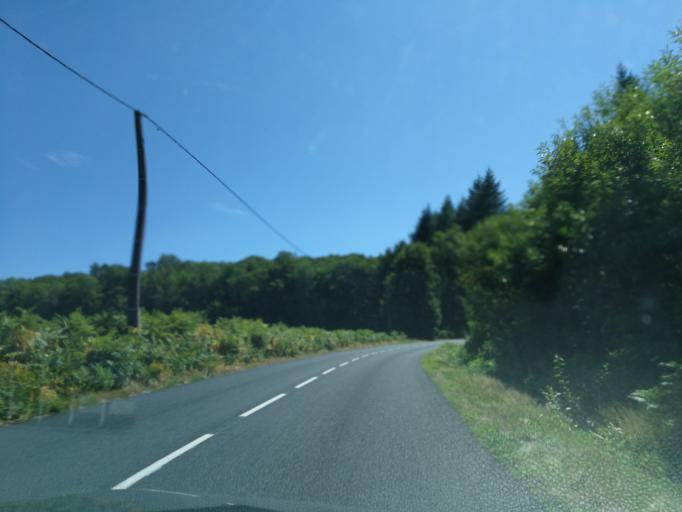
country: FR
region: Limousin
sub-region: Departement de la Correze
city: Argentat
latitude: 45.0039
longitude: 2.0413
